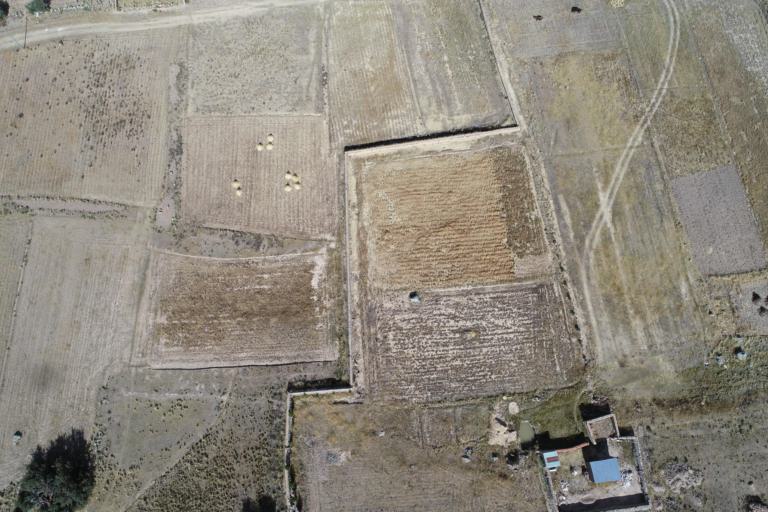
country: BO
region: La Paz
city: Achacachi
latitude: -15.8935
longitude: -68.9082
